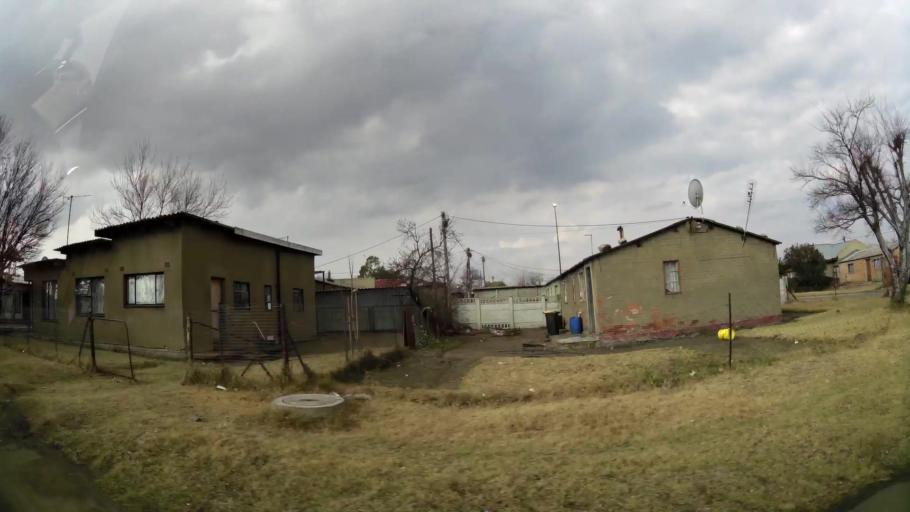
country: ZA
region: Orange Free State
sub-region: Fezile Dabi District Municipality
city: Sasolburg
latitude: -26.8411
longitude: 27.8401
